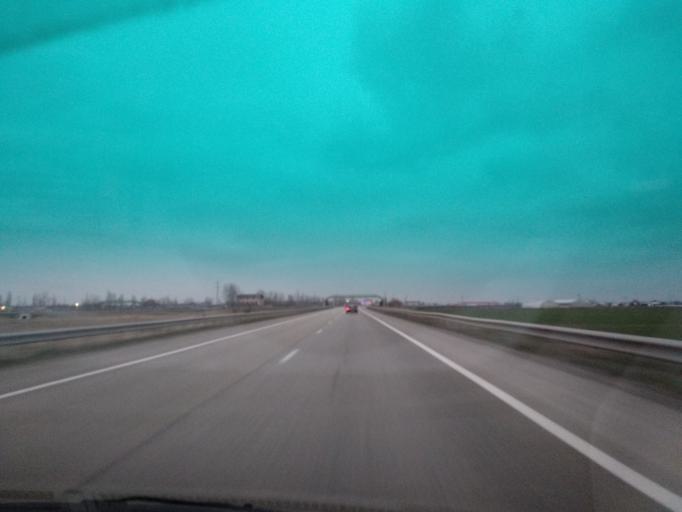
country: RU
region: Adygeya
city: Adygeysk
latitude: 44.8908
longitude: 39.1682
